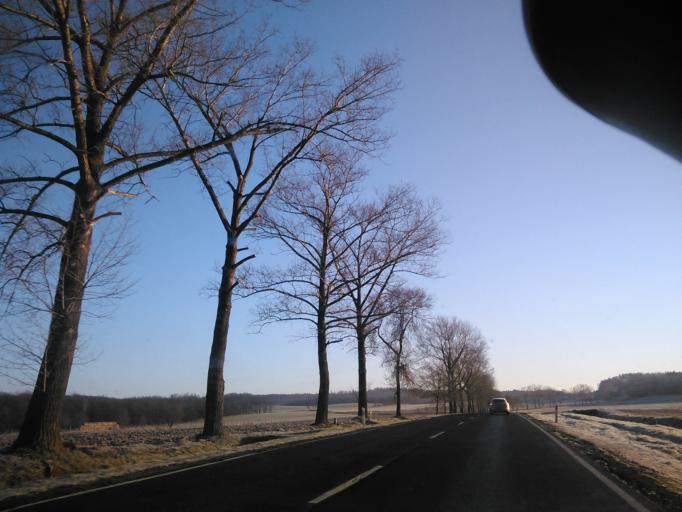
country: PL
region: Lower Silesian Voivodeship
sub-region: Powiat jaworski
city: Bolkow
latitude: 50.9126
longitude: 16.1695
